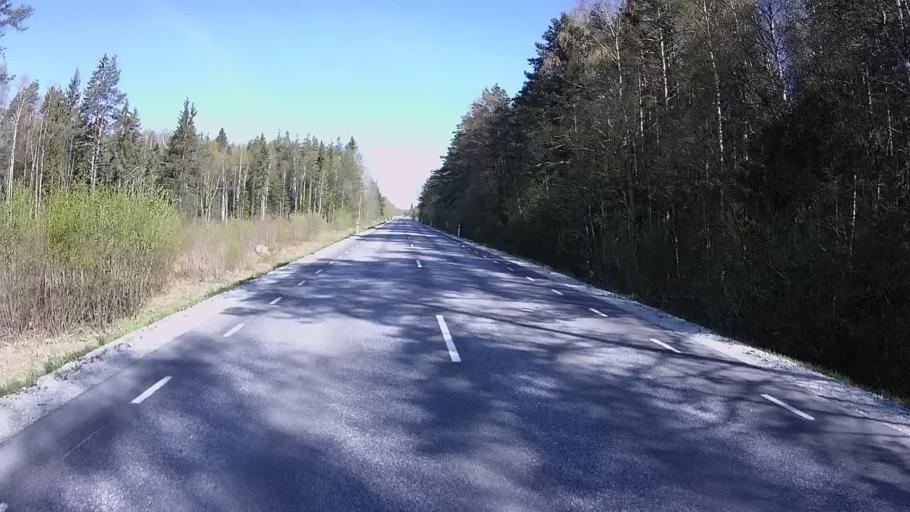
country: EE
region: Raplamaa
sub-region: Jaervakandi vald
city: Jarvakandi
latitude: 58.8634
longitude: 24.7872
